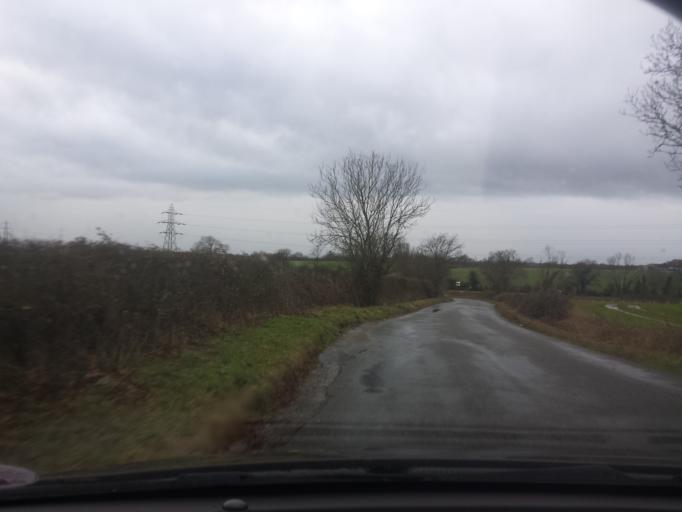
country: GB
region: England
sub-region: Essex
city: Great Bentley
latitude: 51.8936
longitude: 1.0925
